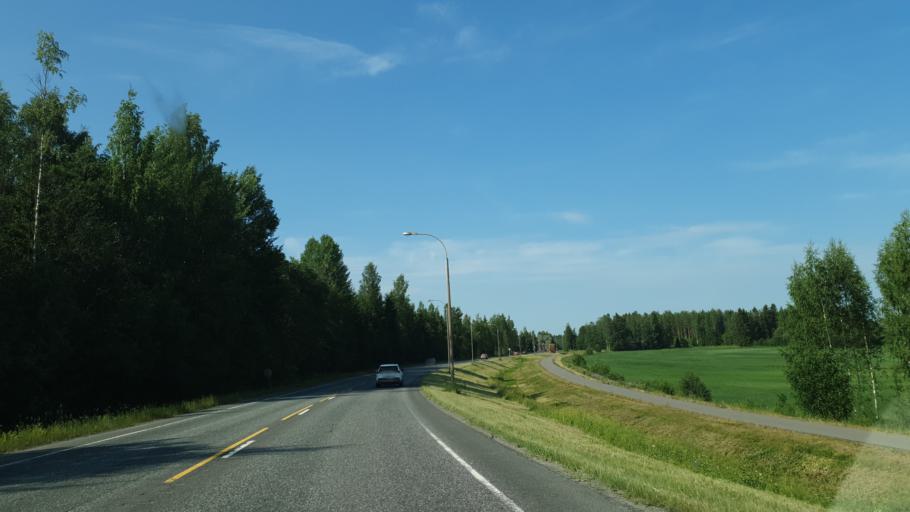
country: FI
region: Northern Savo
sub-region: Kuopio
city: Siilinjaervi
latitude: 63.1221
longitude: 27.7691
